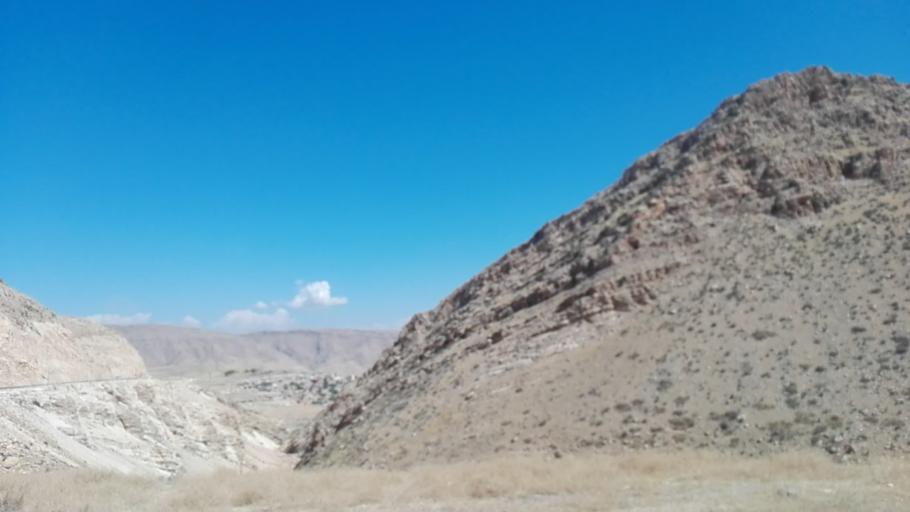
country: TR
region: Batman
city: Hasankeyf
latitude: 37.6972
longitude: 41.4584
